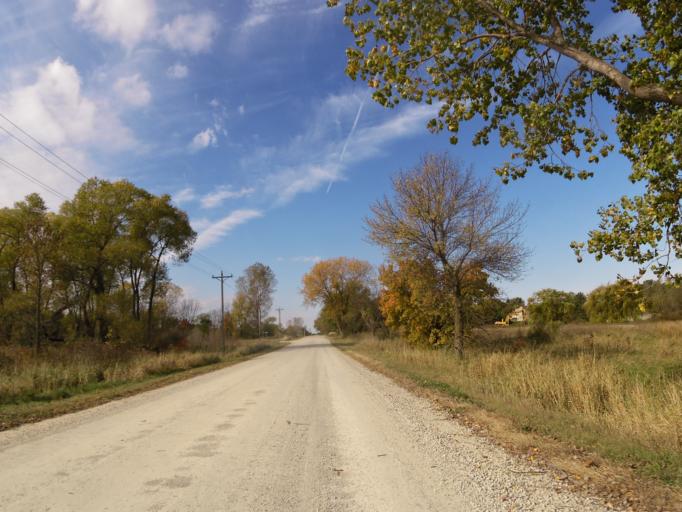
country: US
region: Minnesota
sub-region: Scott County
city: Prior Lake
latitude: 44.6887
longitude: -93.4434
